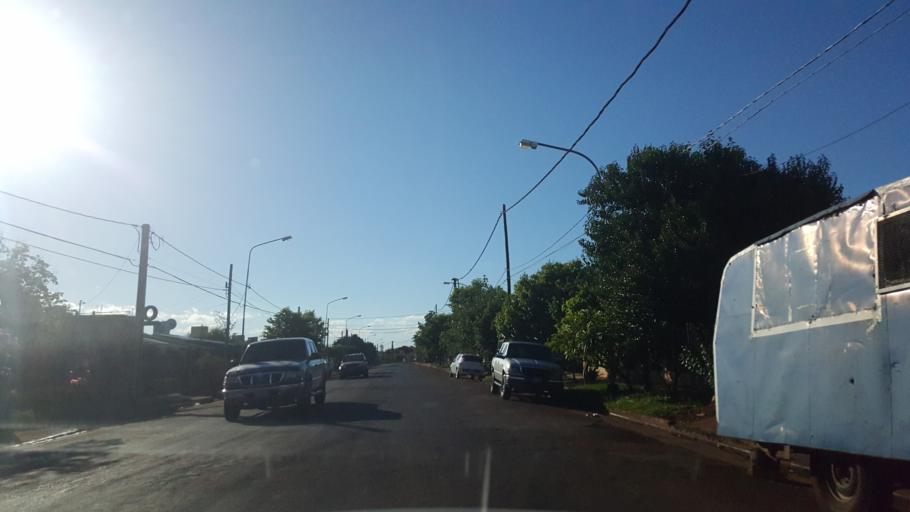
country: AR
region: Misiones
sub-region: Departamento de Capital
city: Posadas
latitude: -27.4300
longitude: -55.9472
